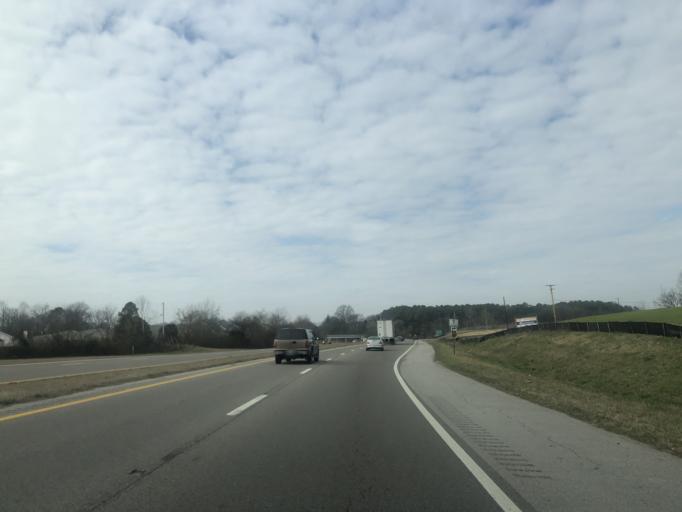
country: US
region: Tennessee
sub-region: Maury County
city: Columbia
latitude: 35.6380
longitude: -87.0384
